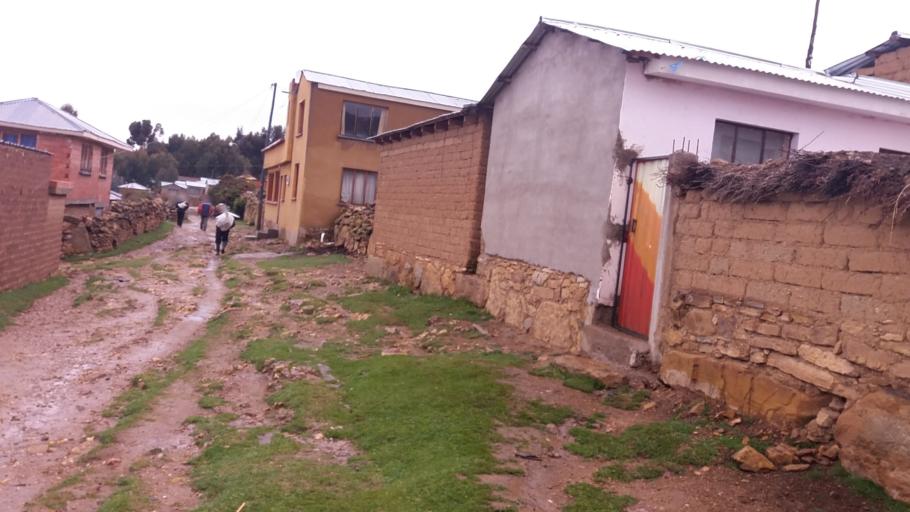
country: BO
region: La Paz
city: Yumani
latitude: -16.0352
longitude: -69.1503
